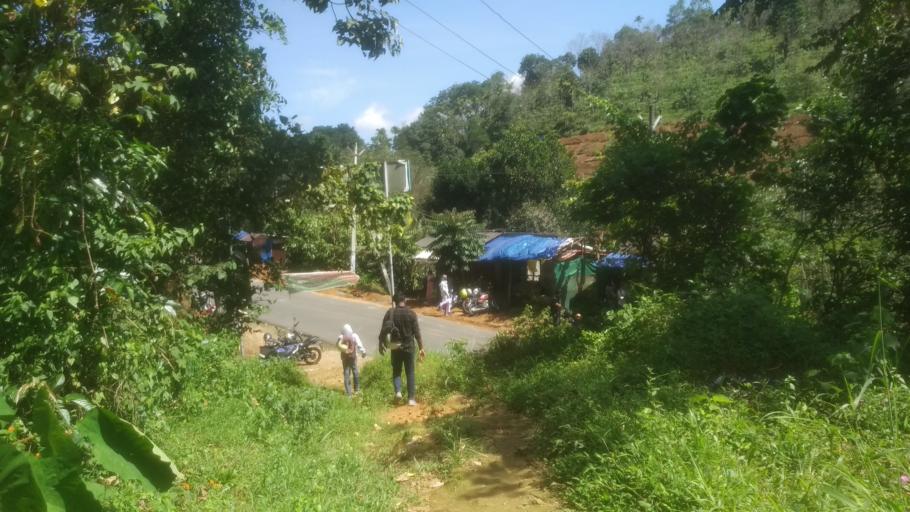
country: IN
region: Kerala
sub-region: Idukki
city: Idukki
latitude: 9.9749
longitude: 76.8384
